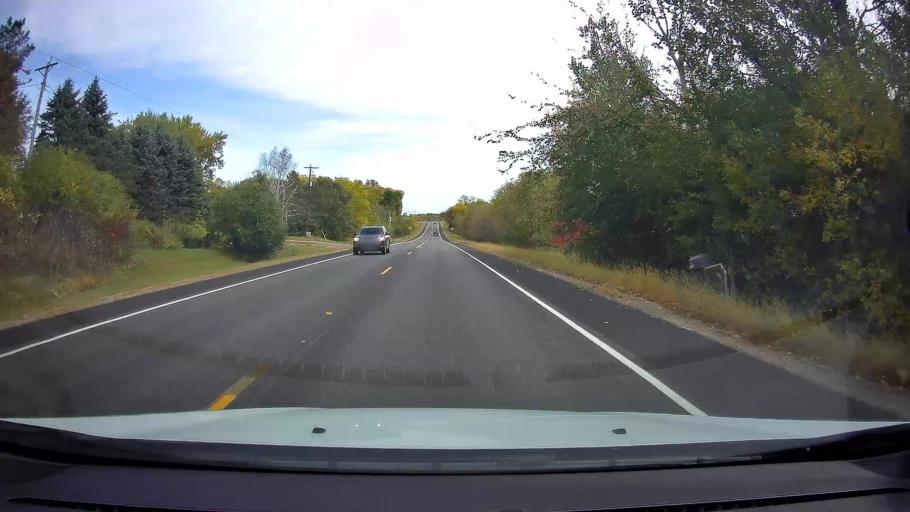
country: US
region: Minnesota
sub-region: Washington County
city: Stillwater
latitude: 45.1167
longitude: -92.7747
